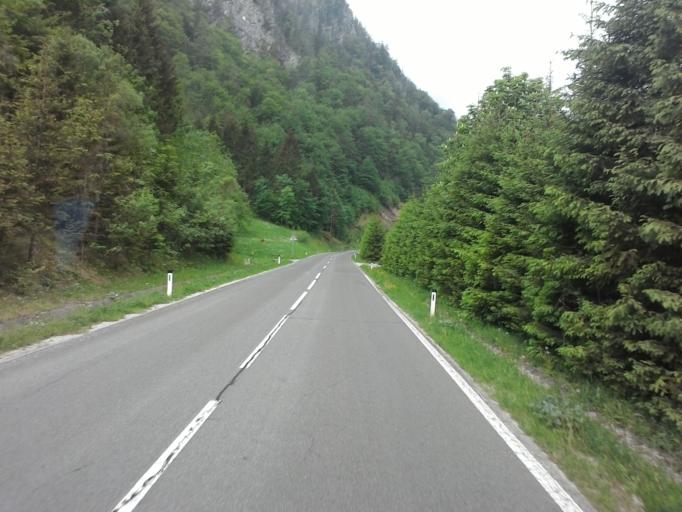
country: AT
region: Styria
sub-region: Politischer Bezirk Liezen
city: Palfau
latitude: 47.6998
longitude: 14.8710
